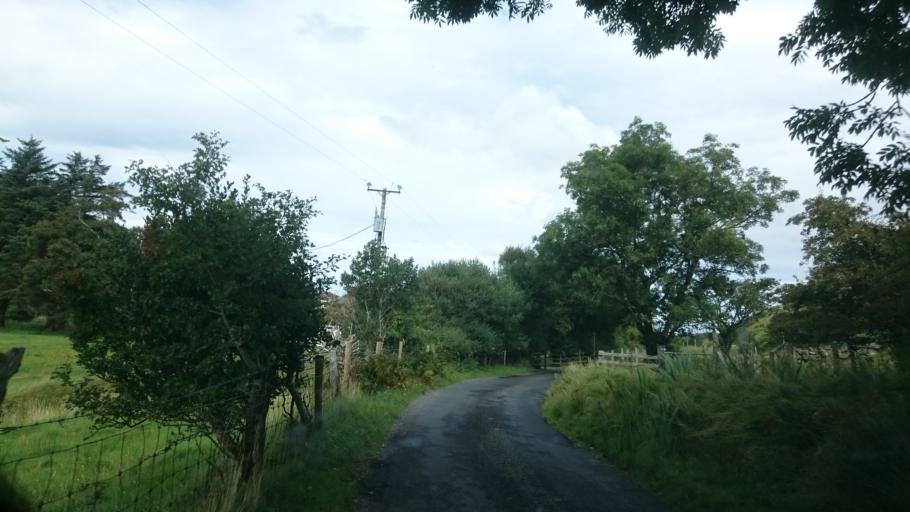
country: IE
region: Connaught
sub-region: Maigh Eo
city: Westport
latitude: 53.9648
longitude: -9.5707
